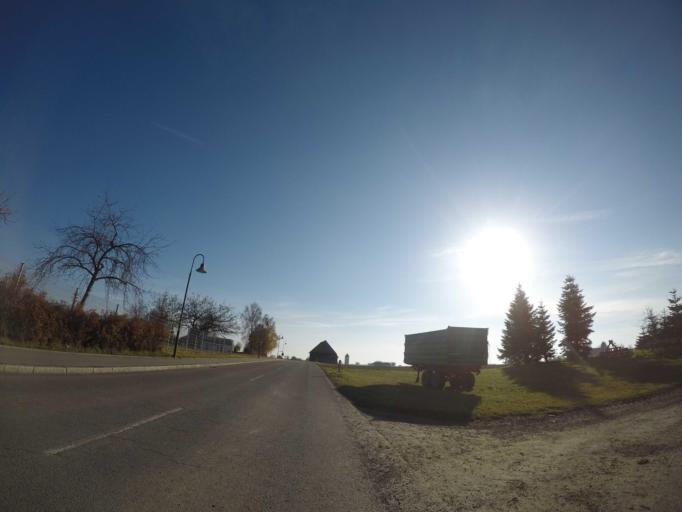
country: DE
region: Baden-Wuerttemberg
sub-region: Tuebingen Region
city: Emerkingen
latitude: 48.2092
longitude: 9.6596
